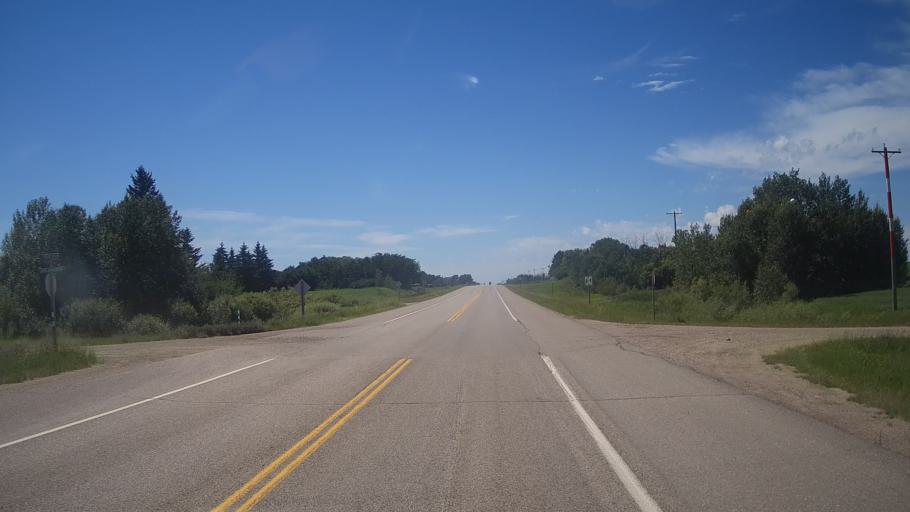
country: CA
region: Saskatchewan
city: Langenburg
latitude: 50.7714
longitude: -101.2987
